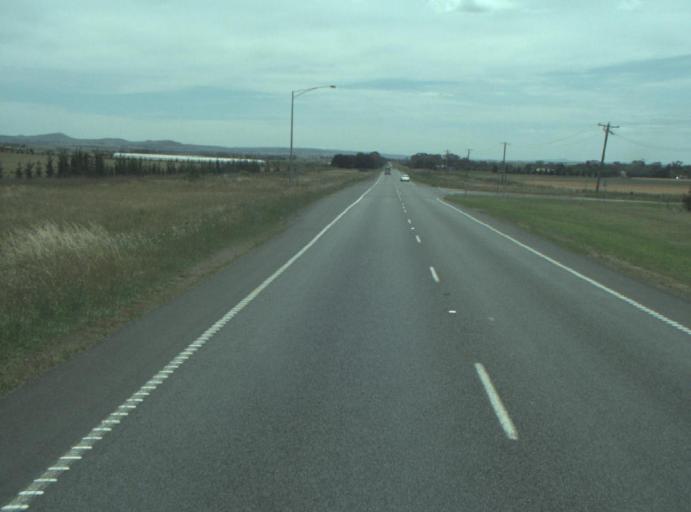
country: AU
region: Victoria
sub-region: Greater Geelong
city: Lara
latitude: -38.0189
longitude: 144.3523
